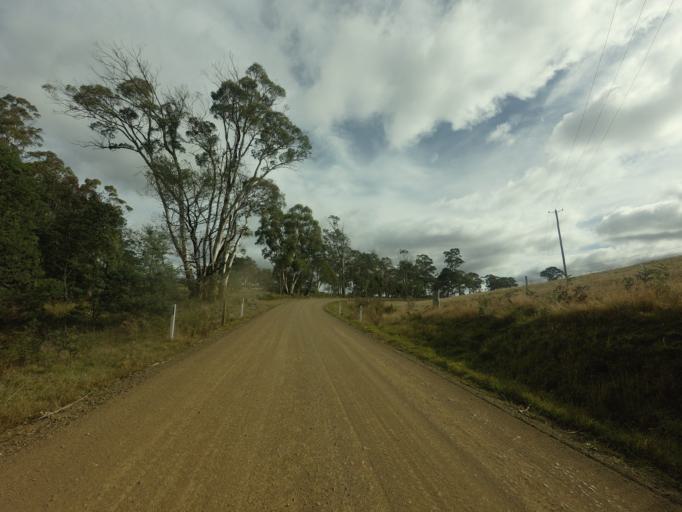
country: AU
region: Tasmania
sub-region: Brighton
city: Bridgewater
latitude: -42.4279
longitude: 147.4337
